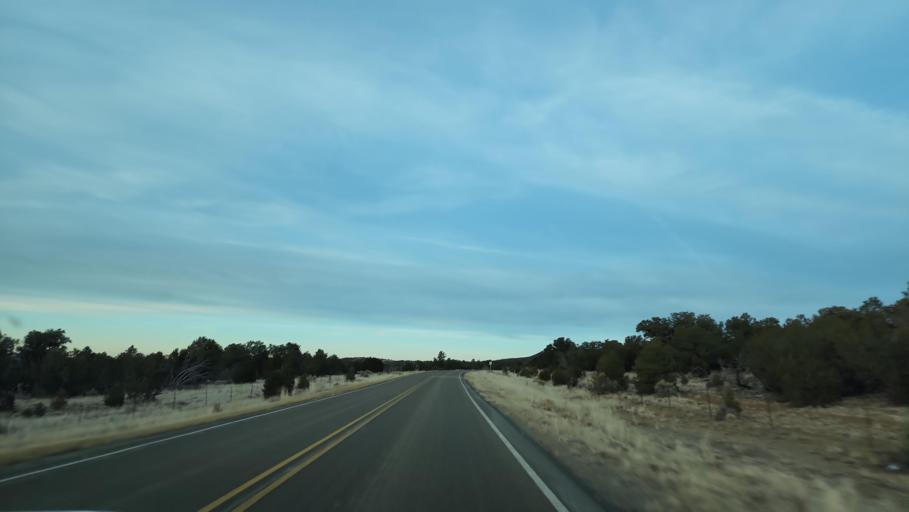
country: US
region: New Mexico
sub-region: Cibola County
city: Grants
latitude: 34.7267
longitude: -107.9743
